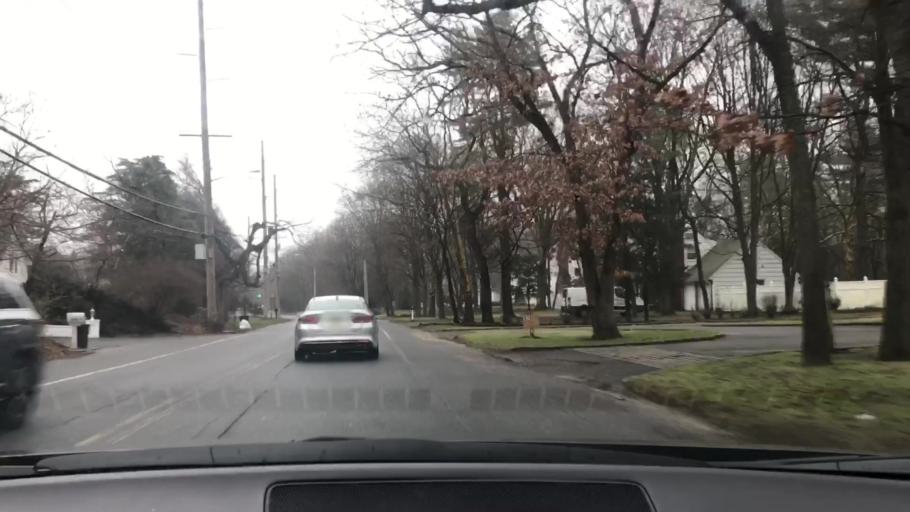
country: US
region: New York
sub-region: Suffolk County
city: South Huntington
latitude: 40.8205
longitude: -73.3730
